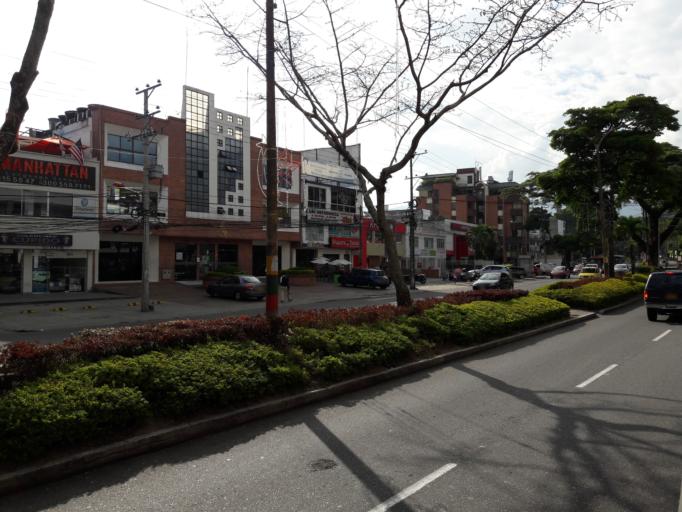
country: CO
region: Tolima
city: Ibague
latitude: 4.4379
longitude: -75.2165
